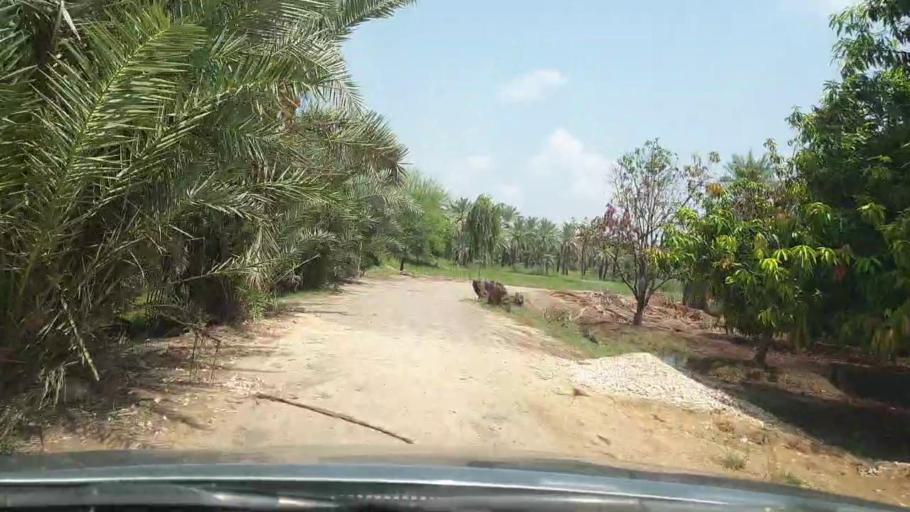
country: PK
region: Sindh
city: Pir jo Goth
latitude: 27.6230
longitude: 68.6653
